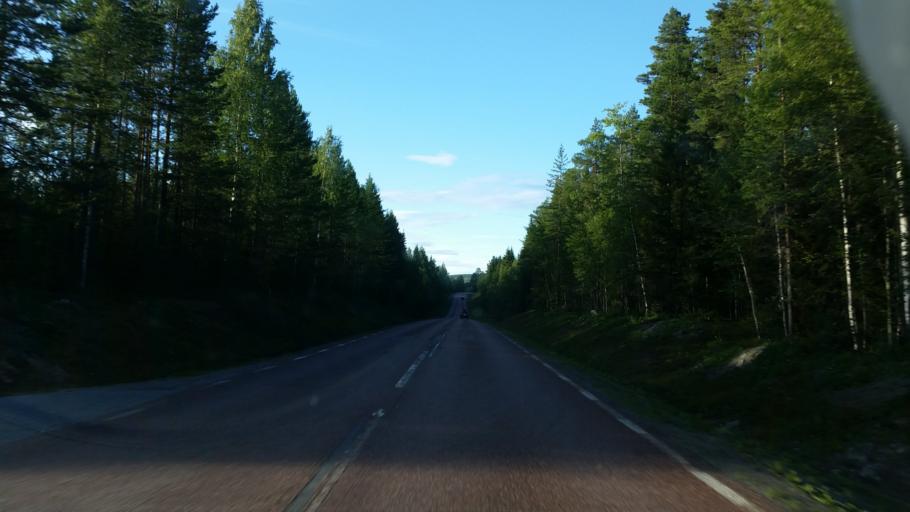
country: SE
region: Vaesterbotten
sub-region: Dorotea Kommun
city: Dorotea
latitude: 64.0954
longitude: 16.0857
